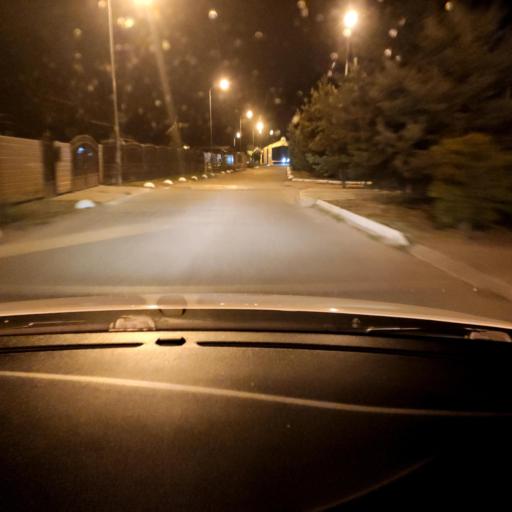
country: RU
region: Tatarstan
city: Osinovo
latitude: 55.8617
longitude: 48.7961
